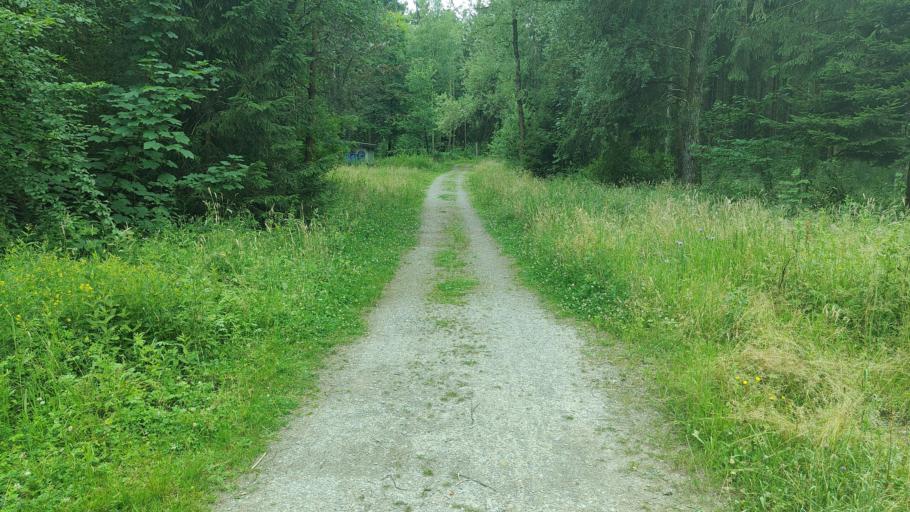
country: BE
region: Wallonia
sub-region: Province de Liege
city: La Calamine
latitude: 50.7160
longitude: 6.0550
